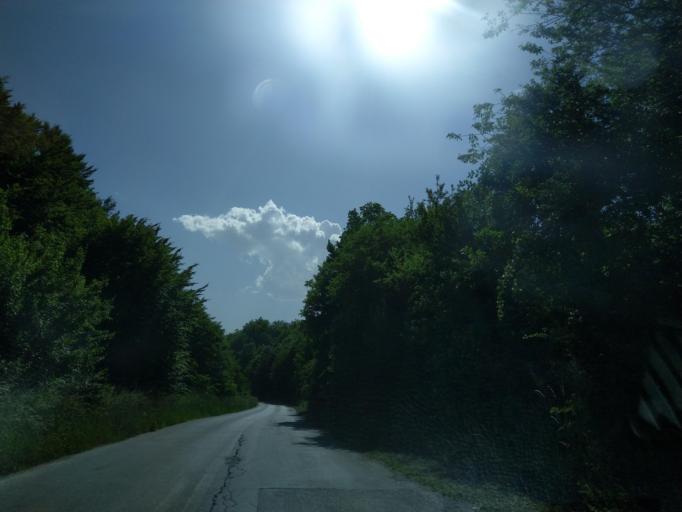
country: RS
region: Central Serbia
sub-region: Zlatiborski Okrug
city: Cajetina
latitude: 43.8719
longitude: 19.7214
